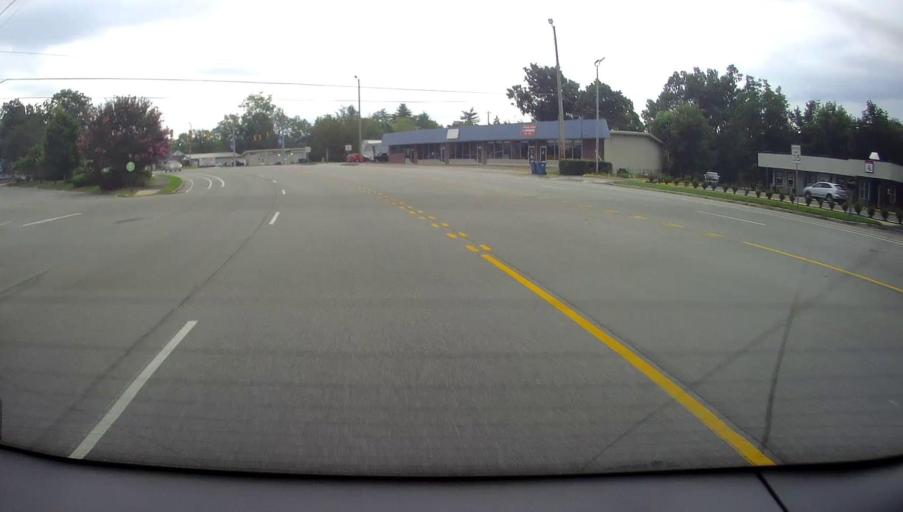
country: US
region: Tennessee
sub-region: Coffee County
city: Manchester
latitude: 35.4821
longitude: -86.0895
